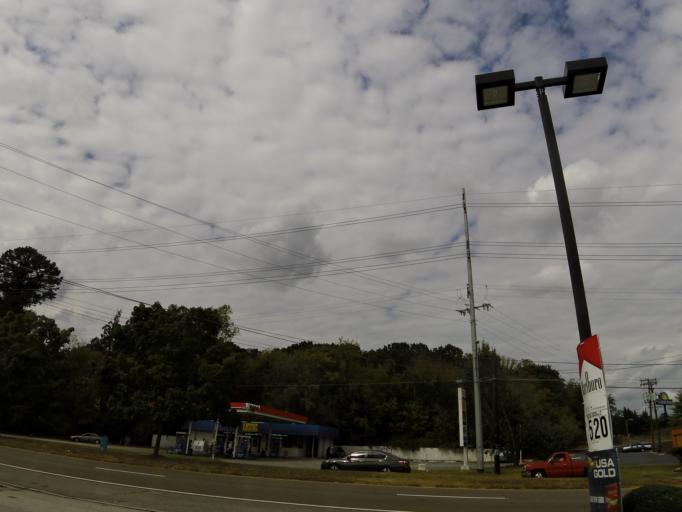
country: US
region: Tennessee
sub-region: Knox County
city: Knoxville
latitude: 36.0095
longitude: -83.8452
